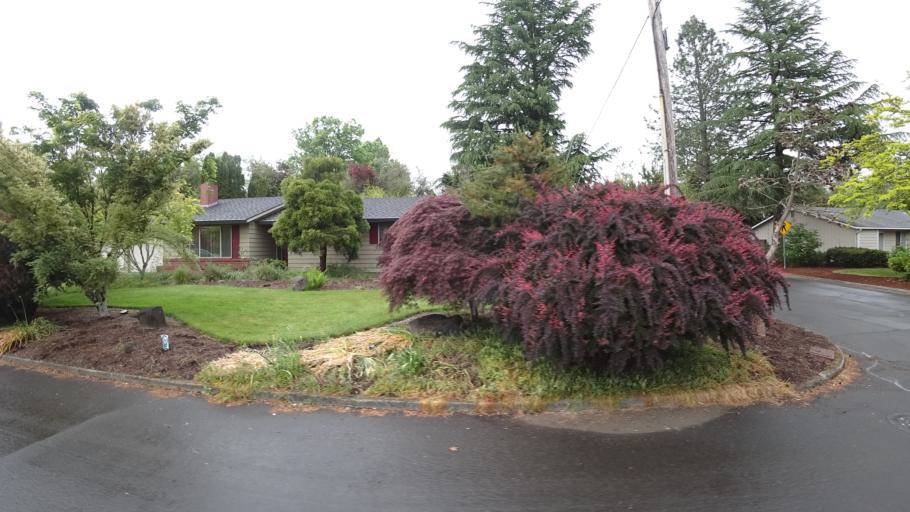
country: US
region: Oregon
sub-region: Washington County
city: Garden Home-Whitford
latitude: 45.4705
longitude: -122.7702
